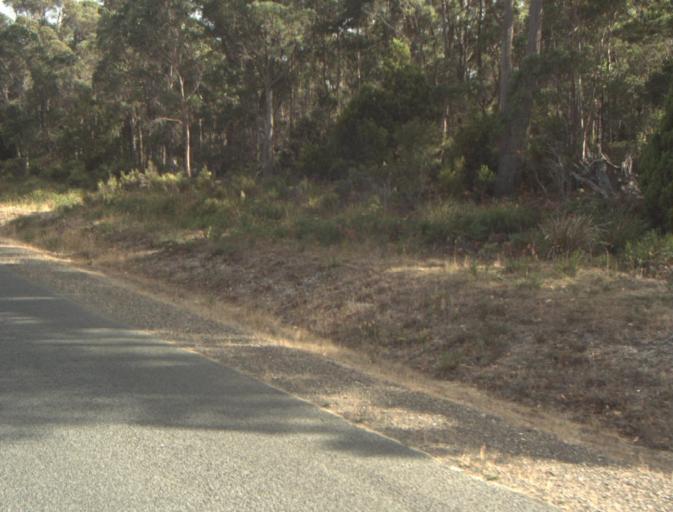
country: AU
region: Tasmania
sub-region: Dorset
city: Bridport
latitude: -41.1296
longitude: 147.2134
